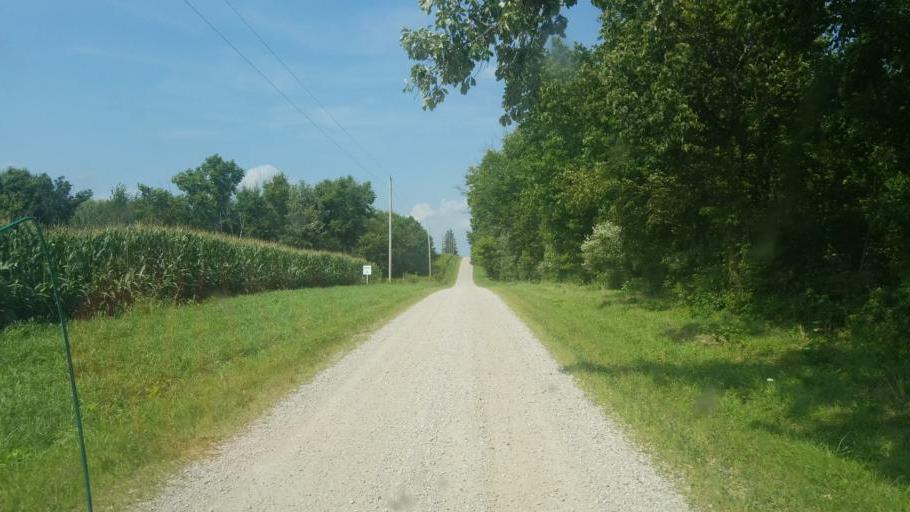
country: US
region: Ohio
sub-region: Huron County
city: New London
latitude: 41.0621
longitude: -82.4100
